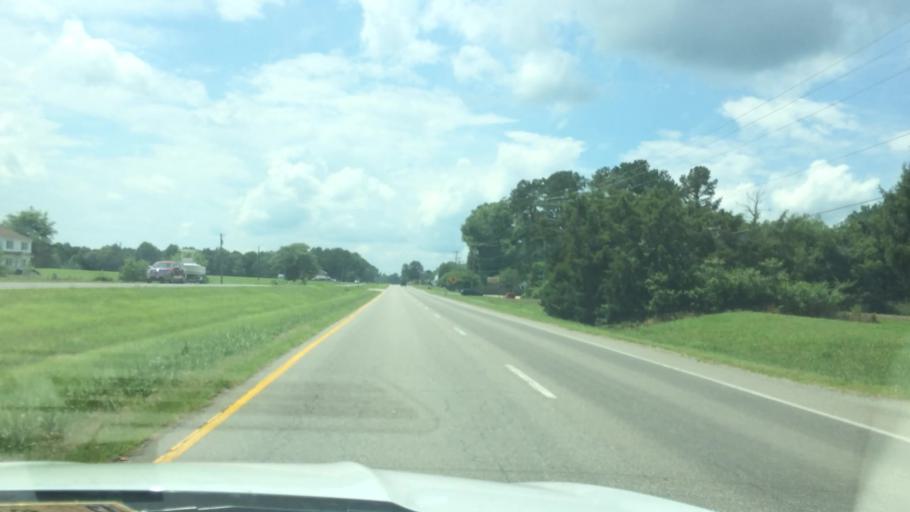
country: US
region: Virginia
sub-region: King William County
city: West Point
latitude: 37.5451
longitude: -76.7098
